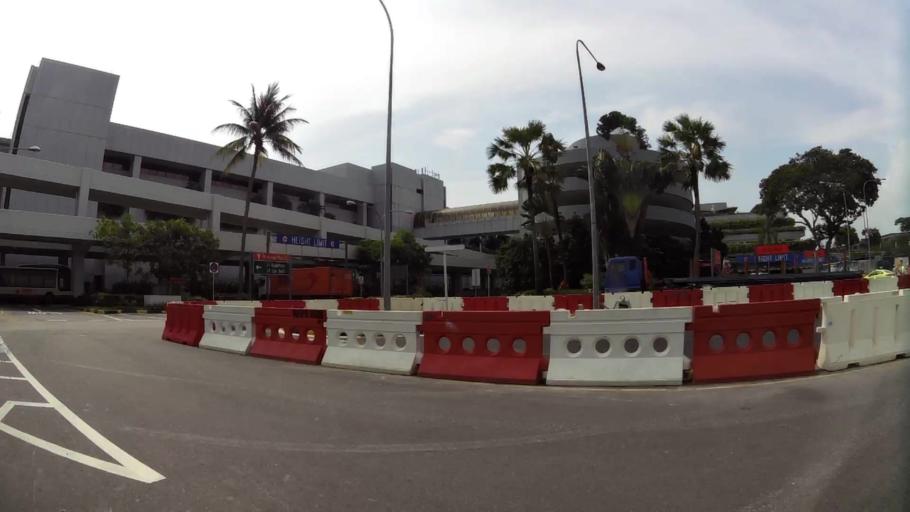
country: SG
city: Singapore
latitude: 1.3590
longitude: 103.9904
